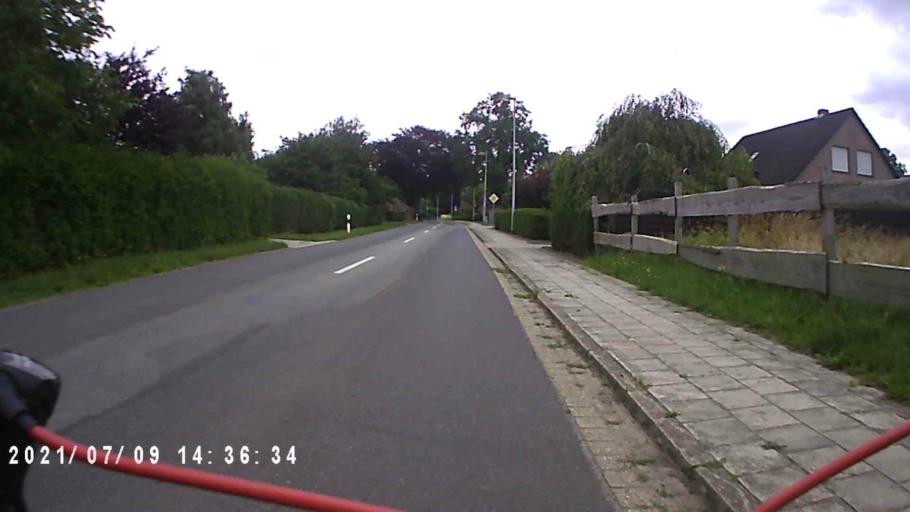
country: DE
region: Lower Saxony
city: Weener
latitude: 53.1138
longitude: 7.3361
